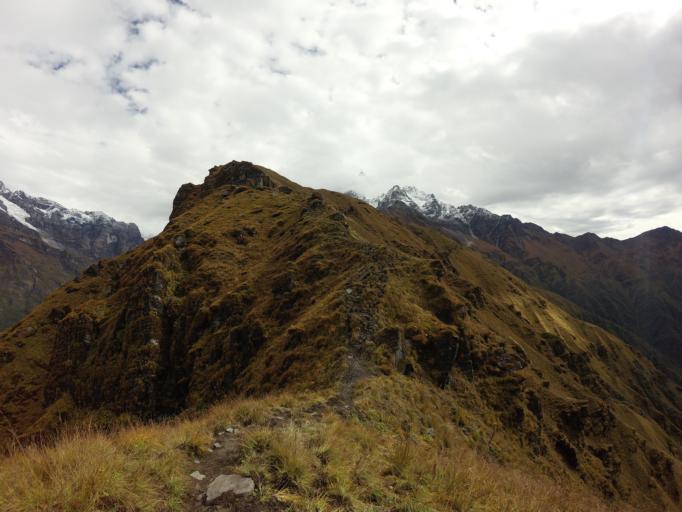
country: NP
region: Western Region
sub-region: Dhawalagiri Zone
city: Chitre
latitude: 28.4535
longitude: 83.8807
